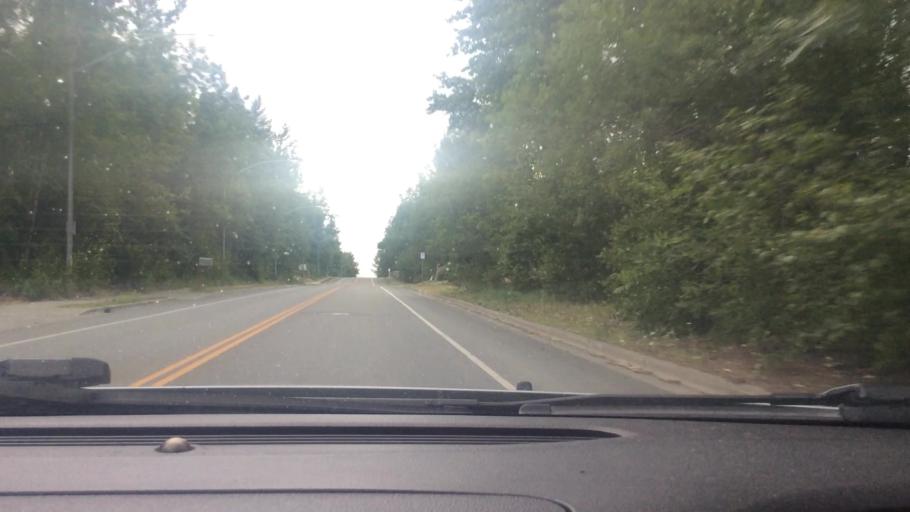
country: US
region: Alaska
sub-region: Anchorage Municipality
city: Anchorage
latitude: 61.1859
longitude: -149.7635
